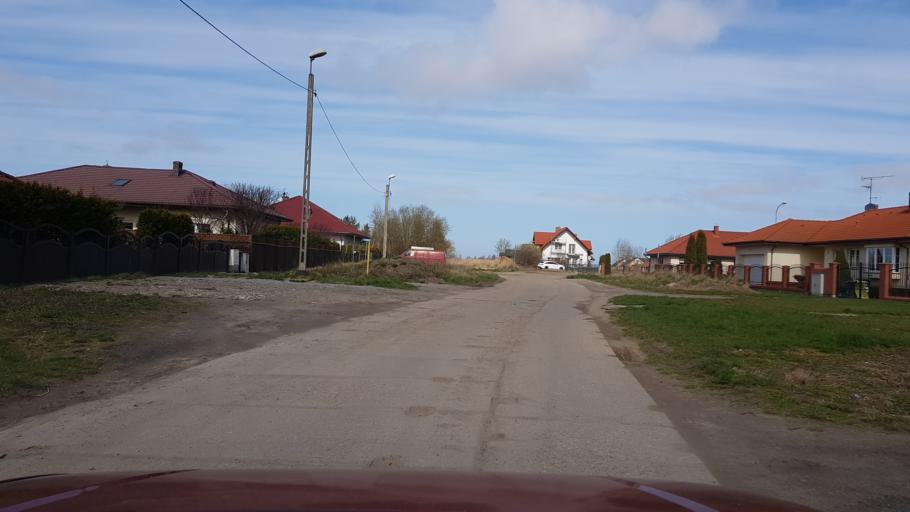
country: PL
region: West Pomeranian Voivodeship
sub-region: Koszalin
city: Koszalin
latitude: 54.2202
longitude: 16.1686
